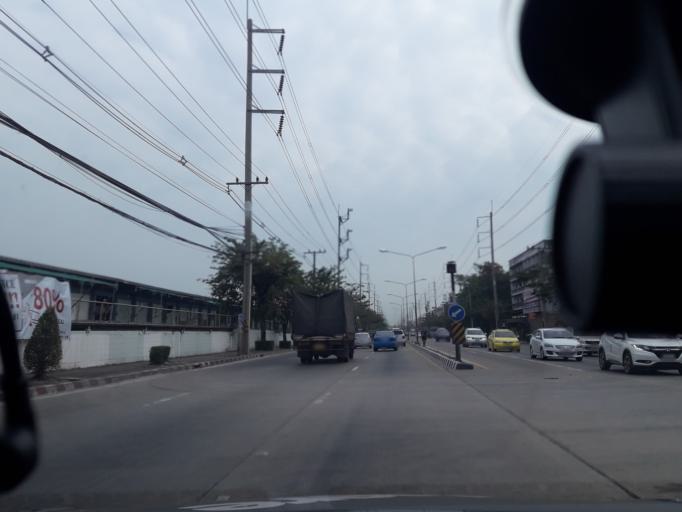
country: TH
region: Pathum Thani
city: Lam Luk Ka
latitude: 13.9344
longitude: 100.7300
